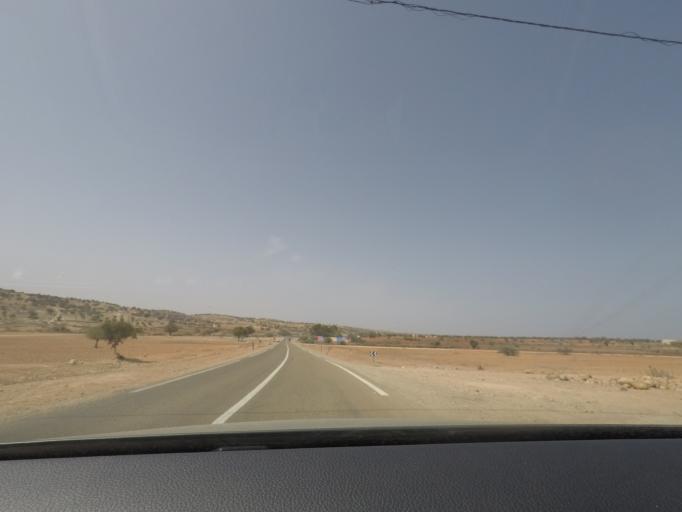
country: MA
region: Marrakech-Tensift-Al Haouz
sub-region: Essaouira
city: Tamanar
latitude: 31.0472
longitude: -9.6646
